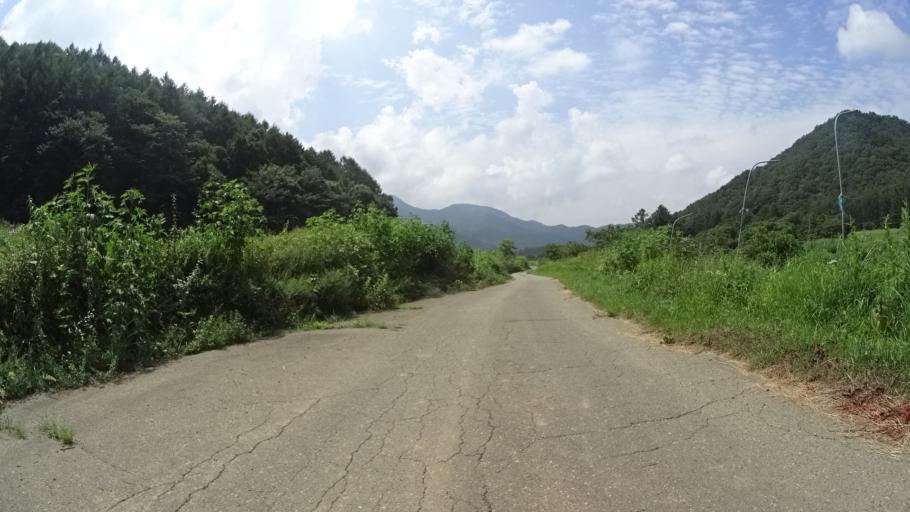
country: JP
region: Yamanashi
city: Nirasaki
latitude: 35.9005
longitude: 138.4710
